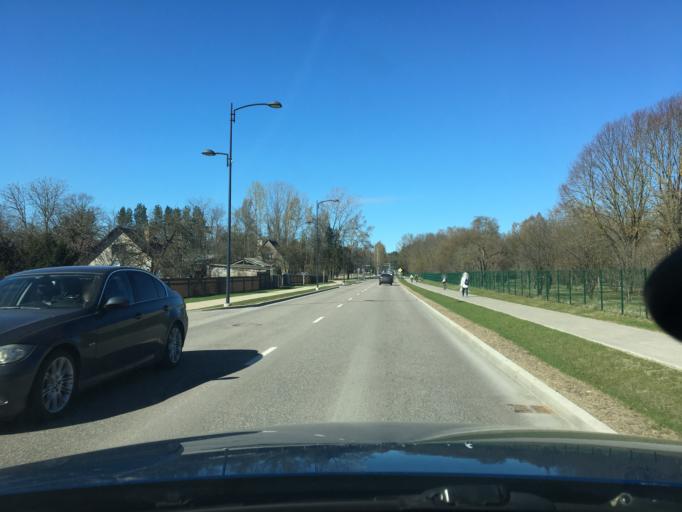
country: LV
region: Salaspils
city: Salaspils
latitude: 56.8660
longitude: 24.3518
